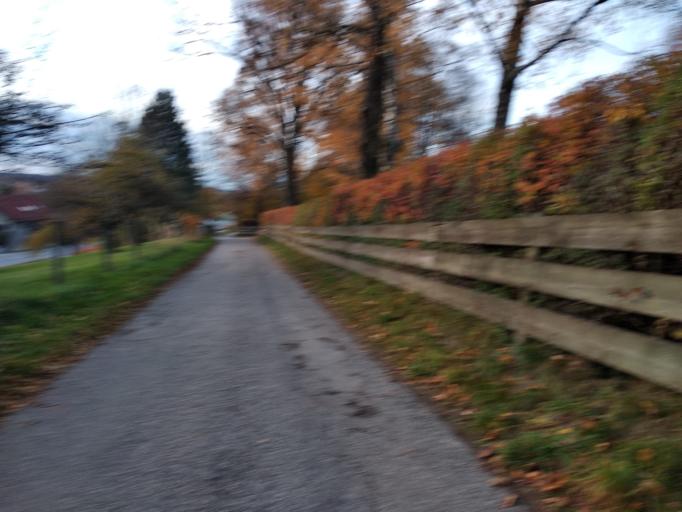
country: DE
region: Bavaria
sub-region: Upper Bavaria
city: Grafing bei Munchen
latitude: 48.0376
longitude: 11.9795
